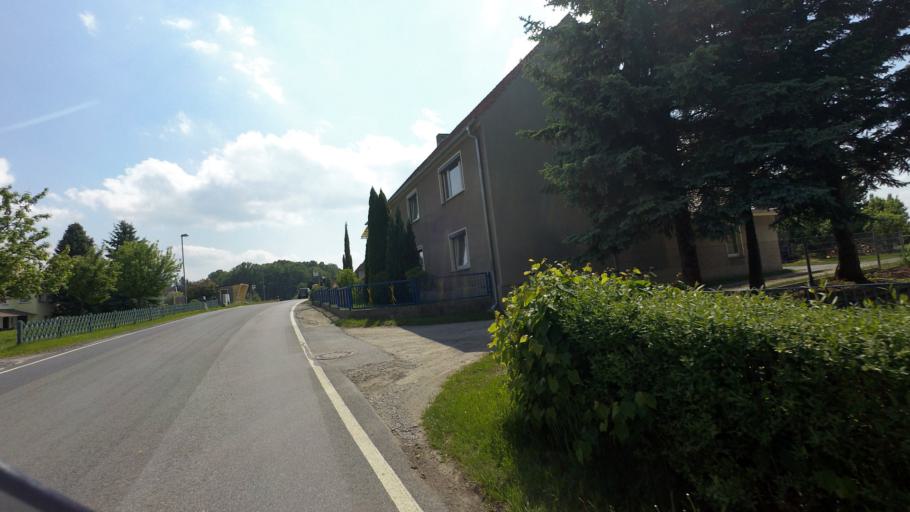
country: DE
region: Saxony
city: Weissenberg
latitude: 51.2557
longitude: 14.6609
